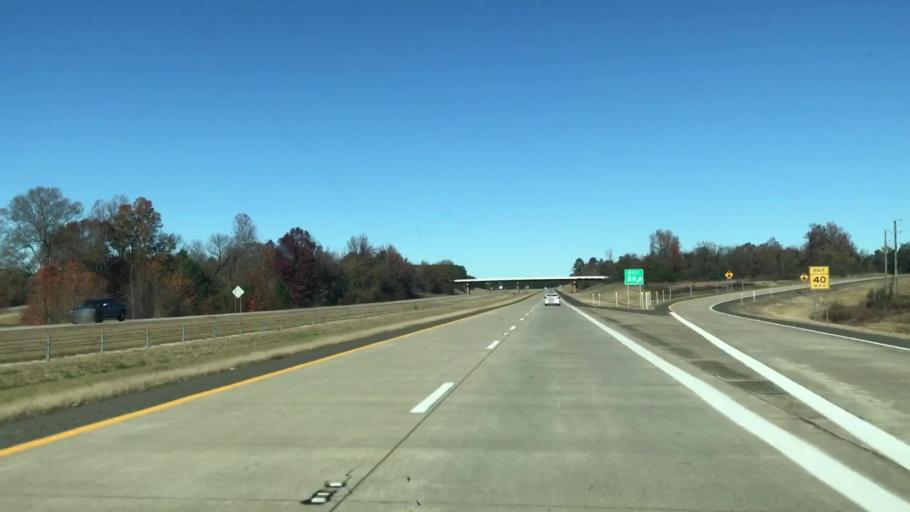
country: US
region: Texas
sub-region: Bowie County
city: Texarkana
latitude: 33.3284
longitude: -93.9568
